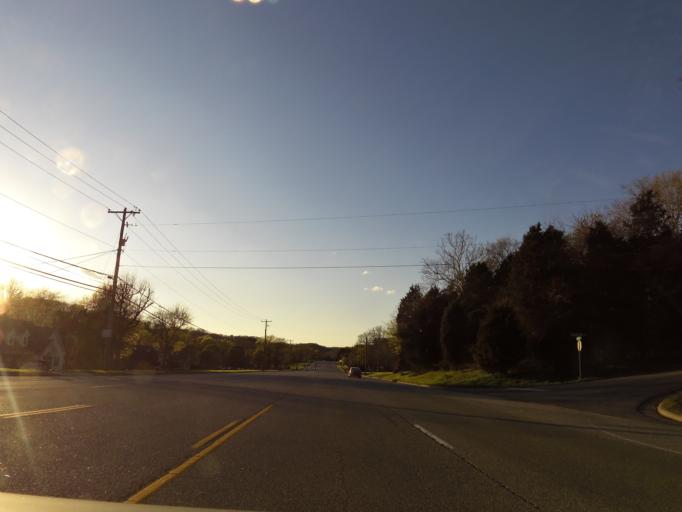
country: US
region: Tennessee
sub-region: Sumner County
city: Millersville
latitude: 36.3672
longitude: -86.7364
